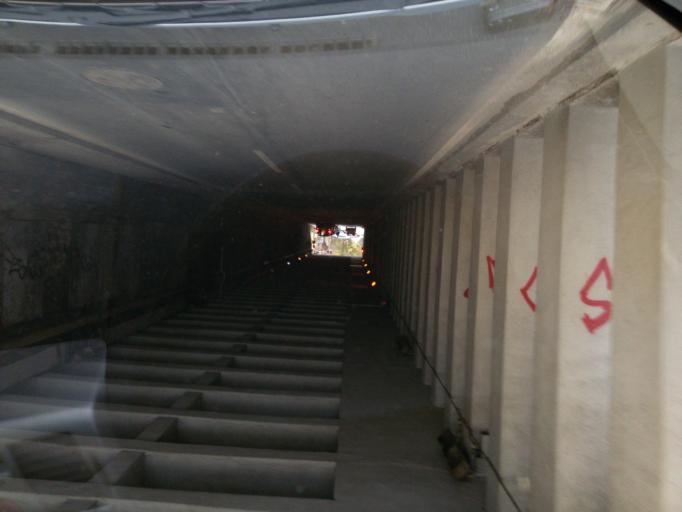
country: IT
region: Liguria
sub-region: Provincia di Genova
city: Genoa
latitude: 44.4058
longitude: 8.9524
